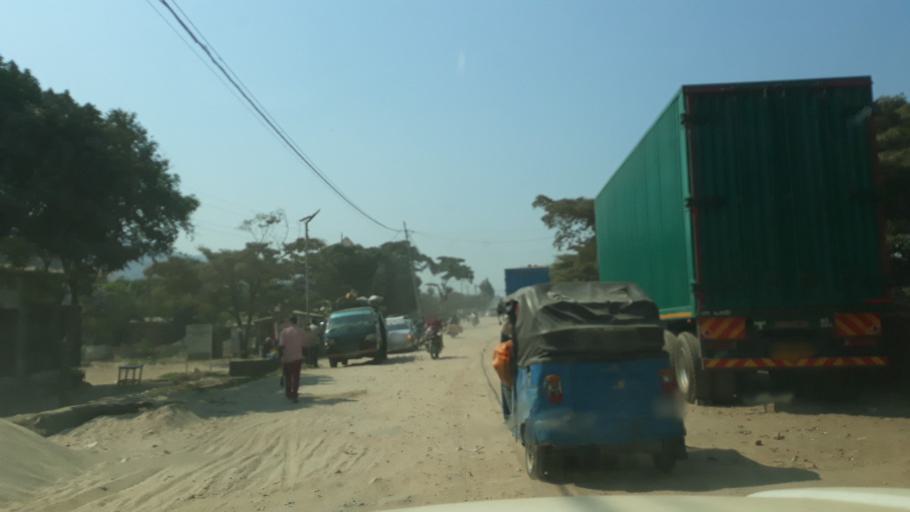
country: CD
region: South Kivu
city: Uvira
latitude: -3.3719
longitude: 29.1460
